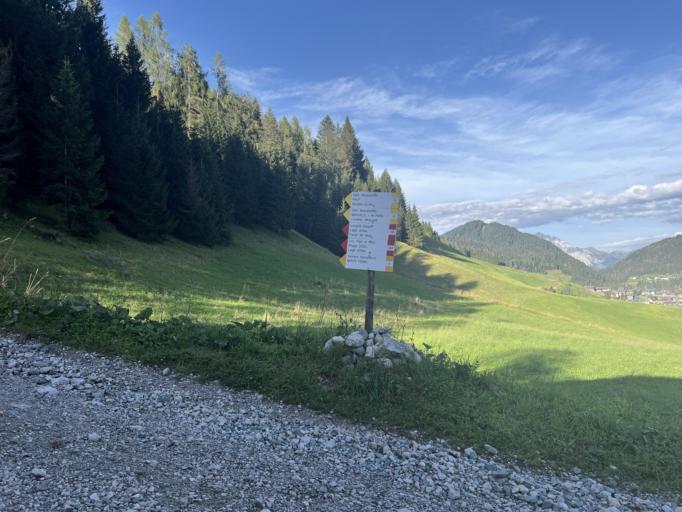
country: IT
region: Veneto
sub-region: Provincia di Belluno
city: Granvilla
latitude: 46.5685
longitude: 12.6889
